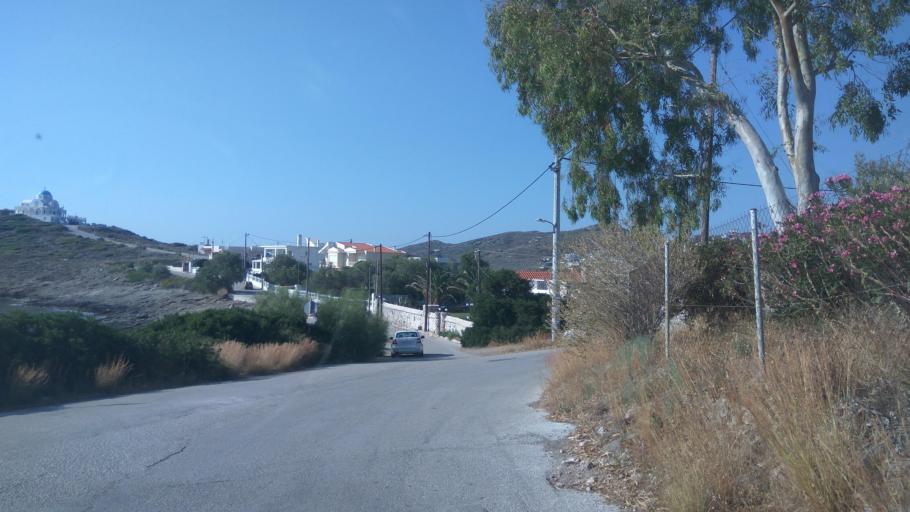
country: GR
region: Attica
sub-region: Nomarchia Anatolikis Attikis
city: Lavrio
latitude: 37.7617
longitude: 24.0758
